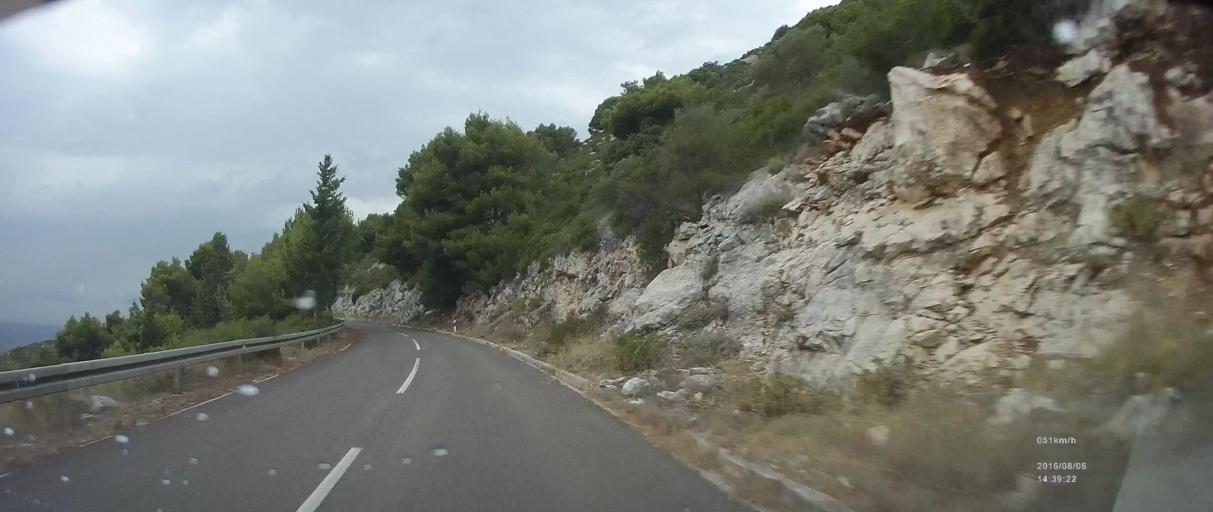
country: HR
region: Dubrovacko-Neretvanska
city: Ston
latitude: 42.7176
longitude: 17.6628
